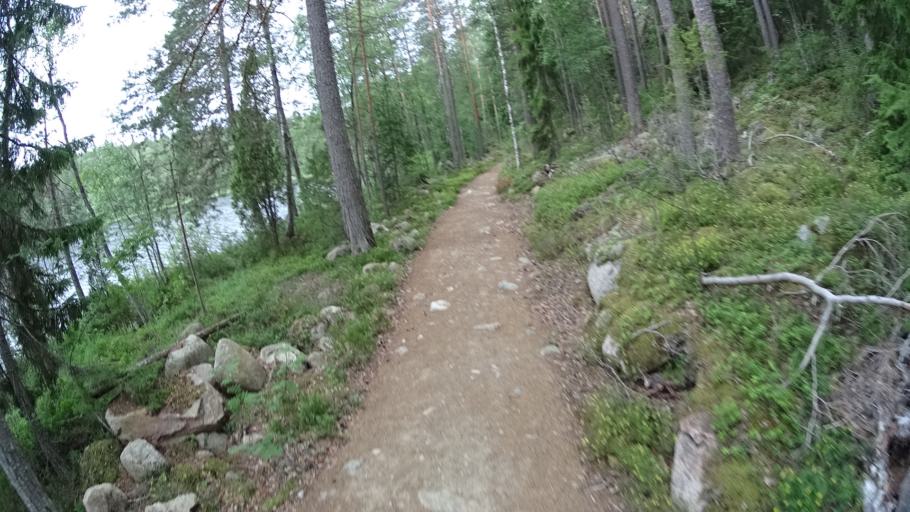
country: FI
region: Southern Savonia
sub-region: Mikkeli
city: Maentyharju
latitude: 61.1791
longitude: 26.8978
